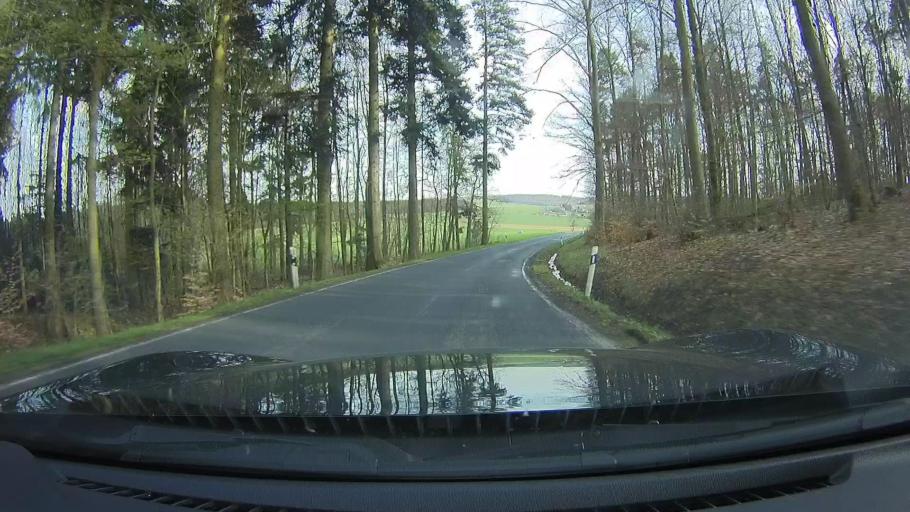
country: DE
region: Bavaria
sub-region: Regierungsbezirk Unterfranken
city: Eichenbuhl
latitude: 49.6476
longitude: 9.3103
